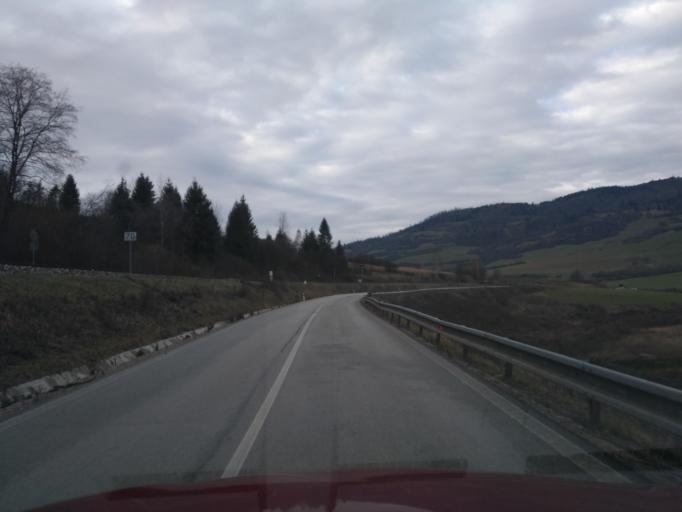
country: SK
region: Kosicky
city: Spisska Nova Ves
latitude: 48.8317
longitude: 20.6481
